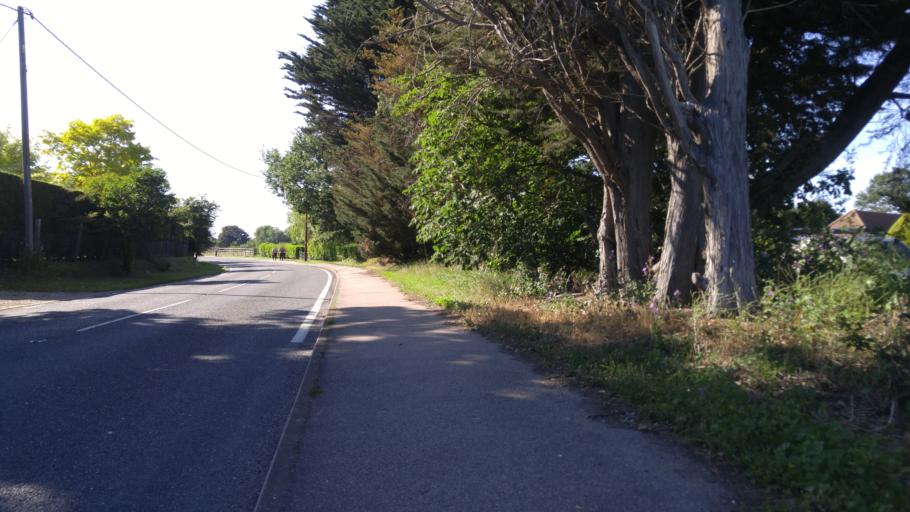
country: GB
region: England
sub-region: Essex
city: Rowhedge
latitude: 51.8629
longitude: 0.9366
